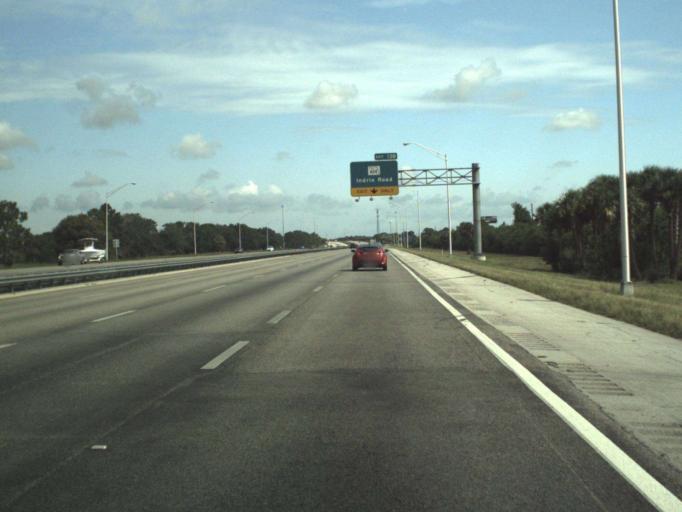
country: US
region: Florida
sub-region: Saint Lucie County
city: Lakewood Park
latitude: 27.5093
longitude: -80.4451
